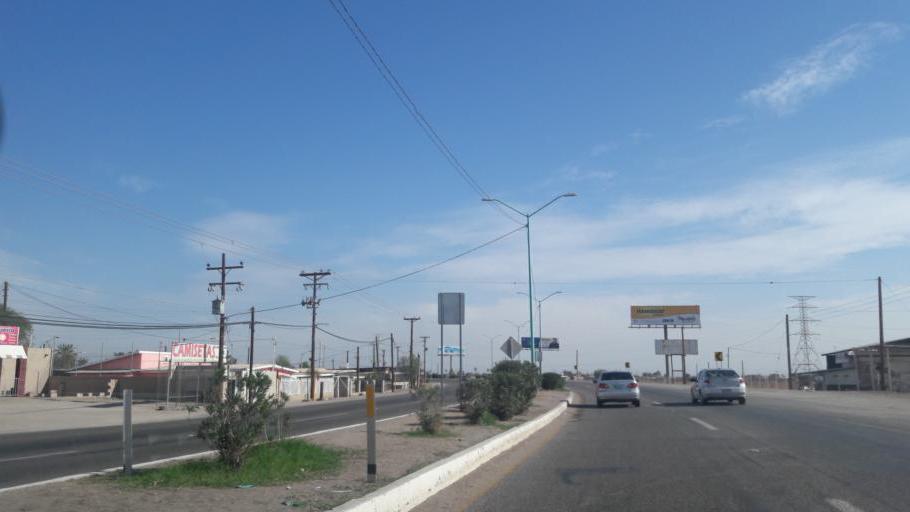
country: MX
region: Baja California
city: Progreso
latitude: 32.5809
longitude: -115.5823
